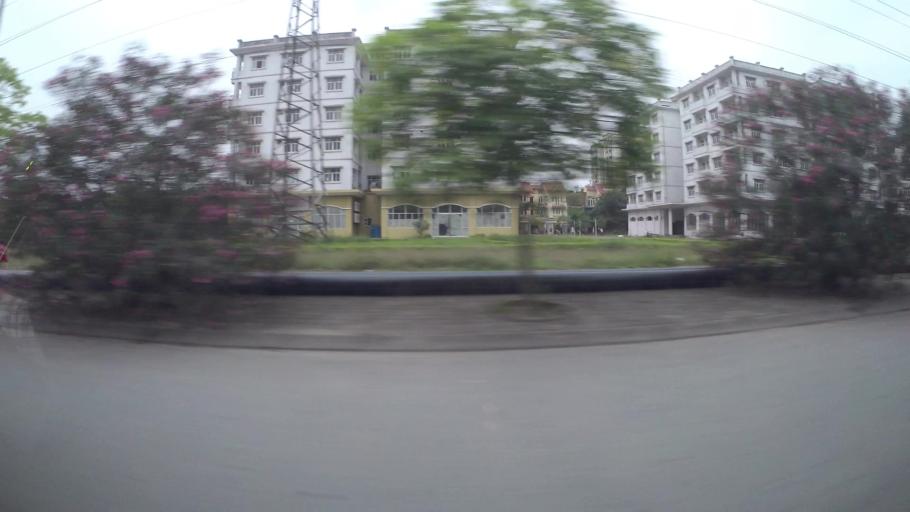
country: VN
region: Ha Noi
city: Trau Quy
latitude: 21.0386
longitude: 105.9073
